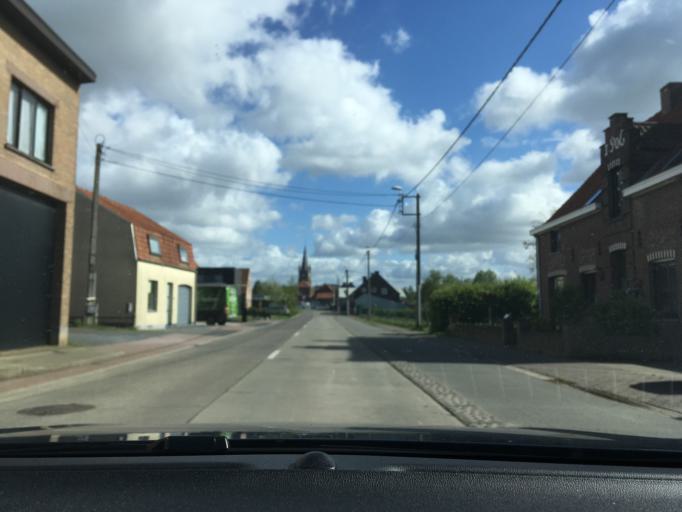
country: BE
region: Flanders
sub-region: Provincie West-Vlaanderen
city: Hooglede
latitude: 51.0004
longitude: 3.0939
